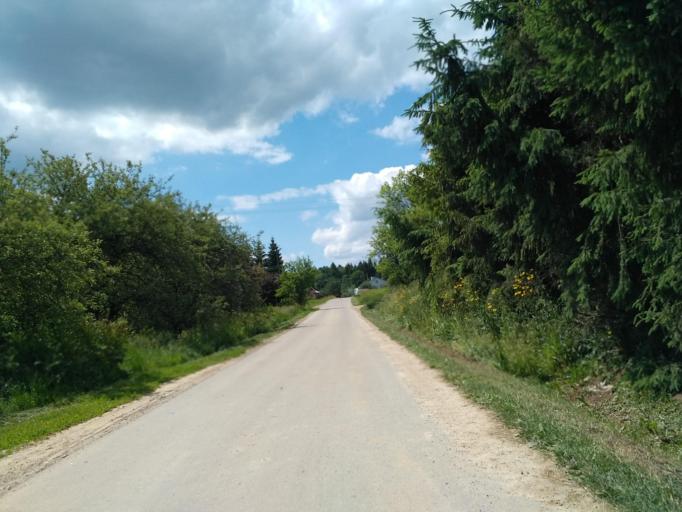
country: PL
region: Subcarpathian Voivodeship
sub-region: Powiat brzozowski
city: Wesola
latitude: 49.7584
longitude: 22.1341
